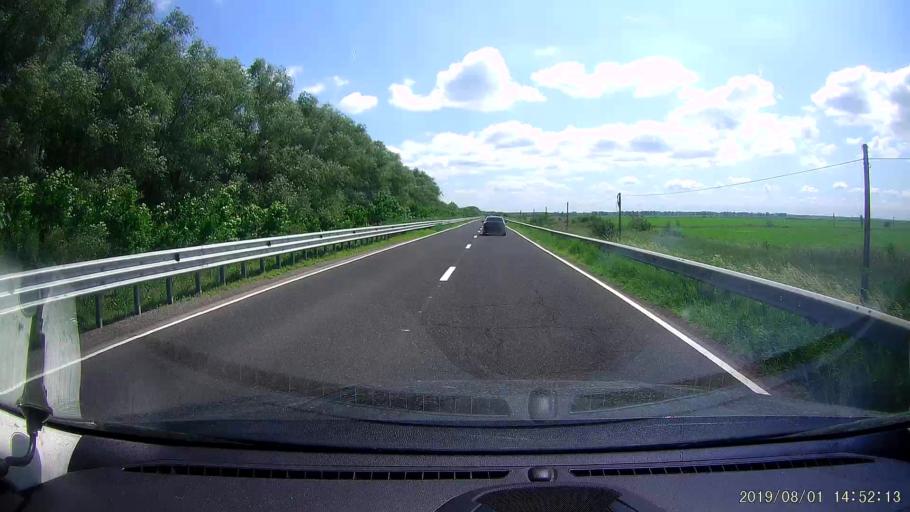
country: RO
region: Braila
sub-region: Comuna Vadeni
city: Vadeni
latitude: 45.3596
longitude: 28.0122
